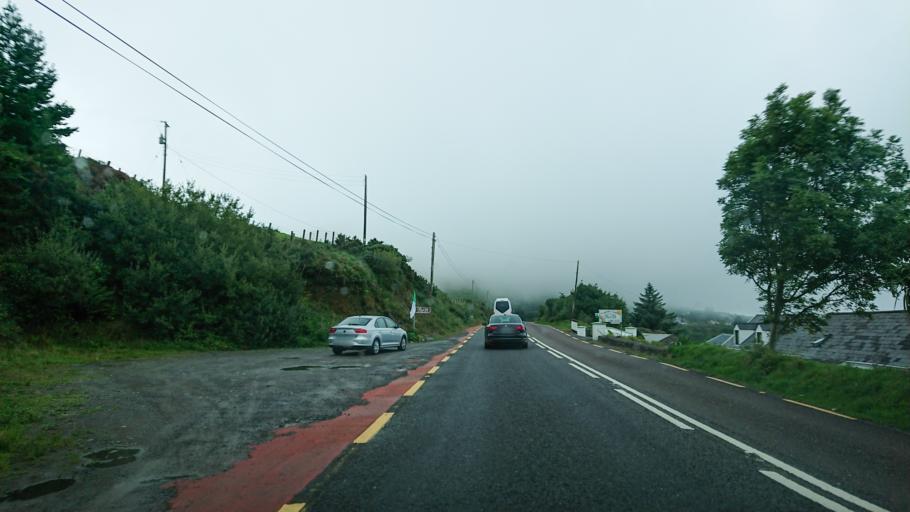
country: IE
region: Munster
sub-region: Ciarrai
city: Cahersiveen
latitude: 52.0353
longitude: -10.0625
